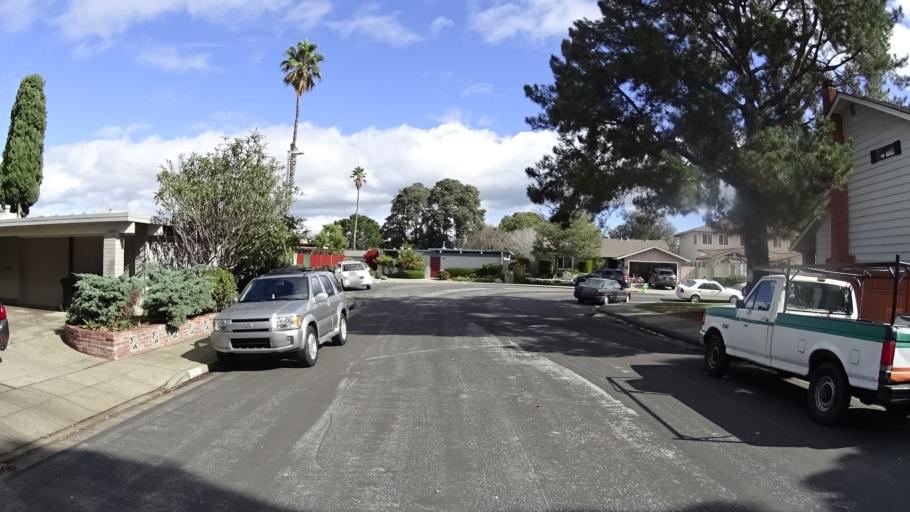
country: US
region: California
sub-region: San Mateo County
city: Foster City
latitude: 37.5607
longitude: -122.2595
